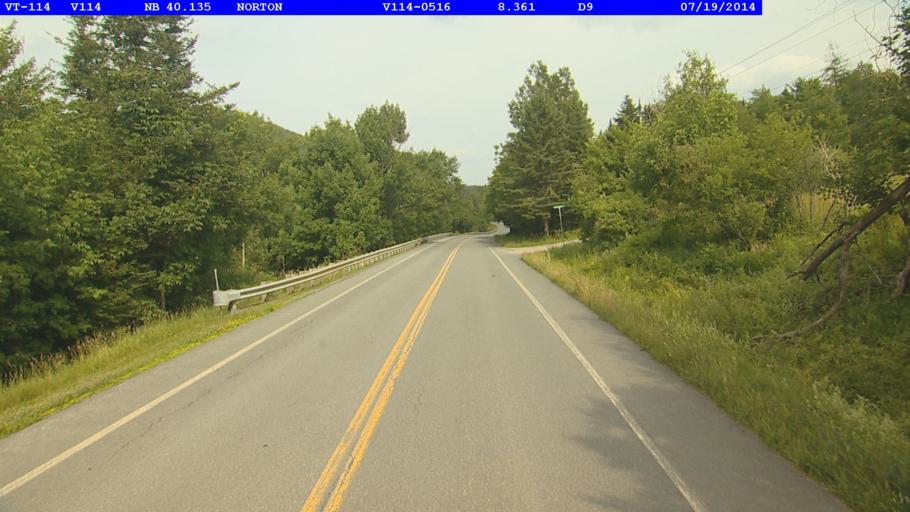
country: CA
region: Quebec
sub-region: Estrie
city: Coaticook
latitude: 44.9960
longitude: -71.7385
